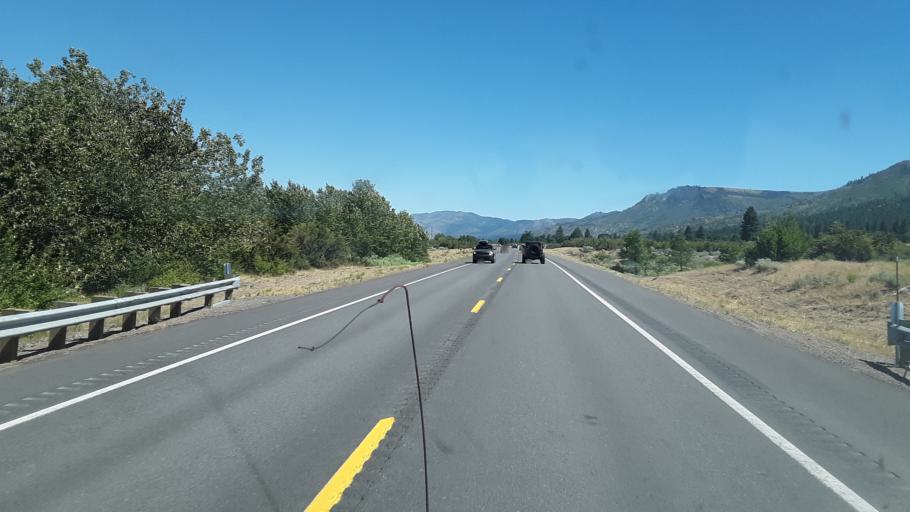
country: US
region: California
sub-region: Lassen County
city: Janesville
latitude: 40.2753
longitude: -120.4830
